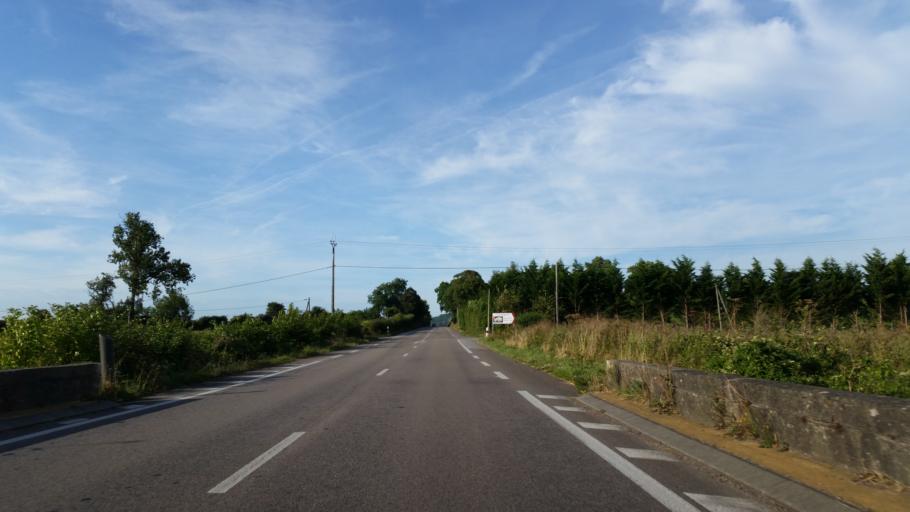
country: FR
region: Lower Normandy
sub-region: Departement du Calvados
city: Cambremer
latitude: 49.1036
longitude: 0.0042
